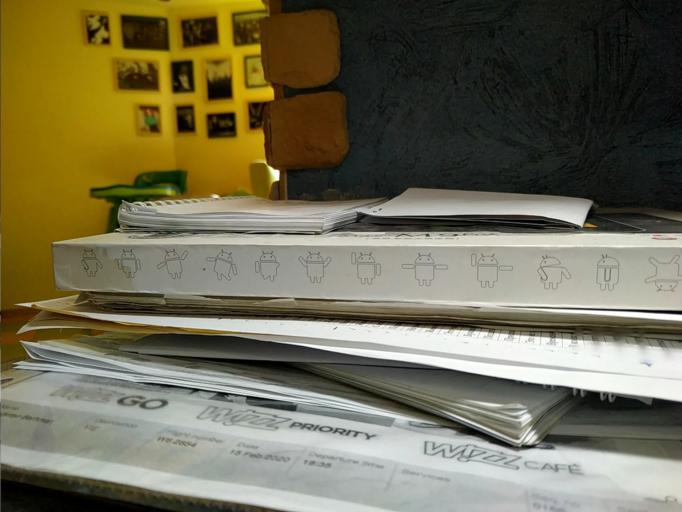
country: RU
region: Novgorod
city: Volot
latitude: 57.8431
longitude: 30.4683
